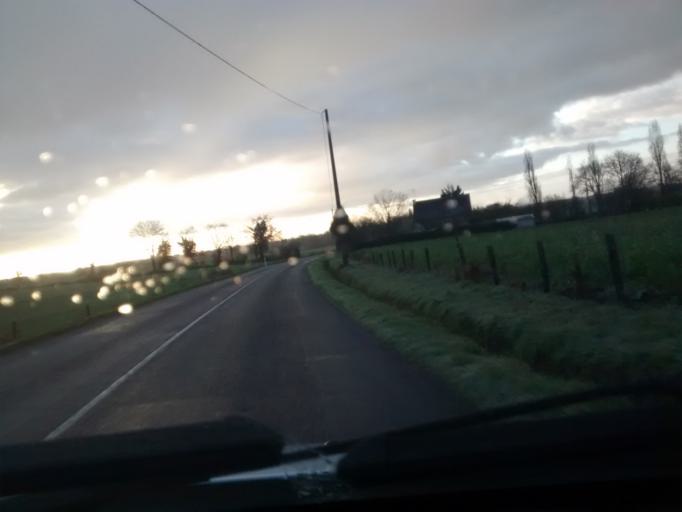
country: FR
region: Brittany
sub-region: Departement d'Ille-et-Vilaine
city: Domalain
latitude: 47.9770
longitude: -1.2715
